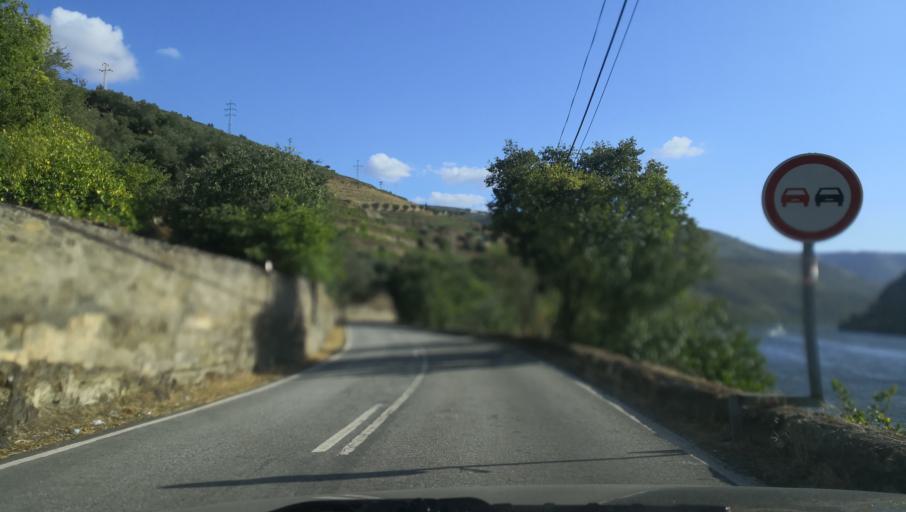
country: PT
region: Viseu
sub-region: Tabuaco
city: Tabuaco
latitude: 41.1804
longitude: -7.5503
